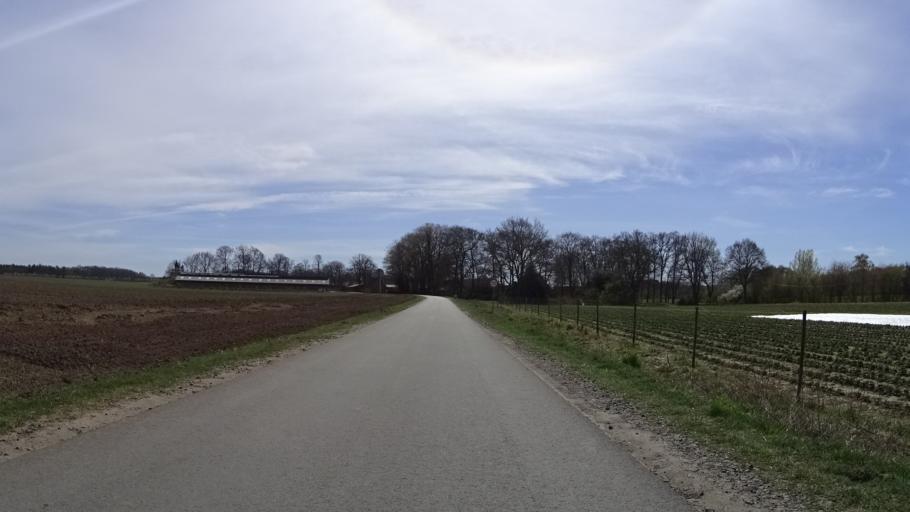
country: DE
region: Lower Saxony
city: Emsburen
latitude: 52.4520
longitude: 7.3350
